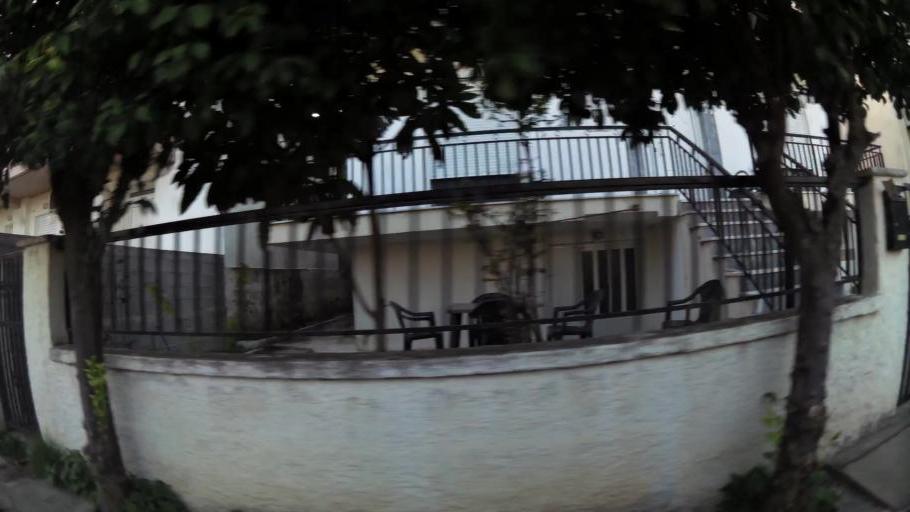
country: GR
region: Attica
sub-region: Nomarchia Anatolikis Attikis
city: Acharnes
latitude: 38.0926
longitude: 23.7418
